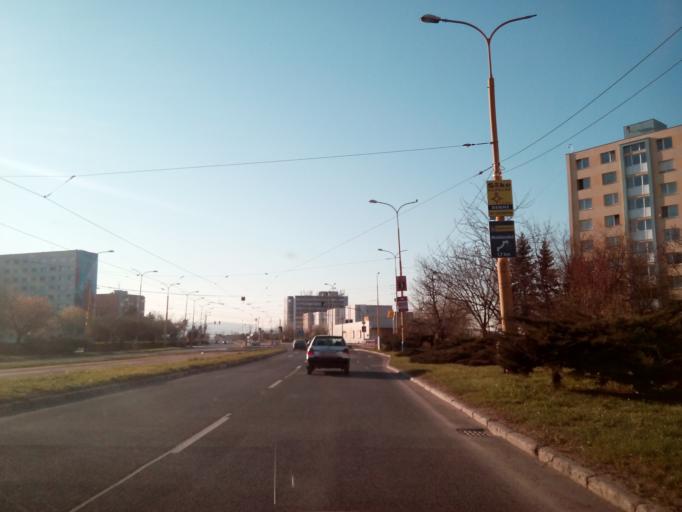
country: SK
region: Kosicky
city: Kosice
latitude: 48.7079
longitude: 21.2382
